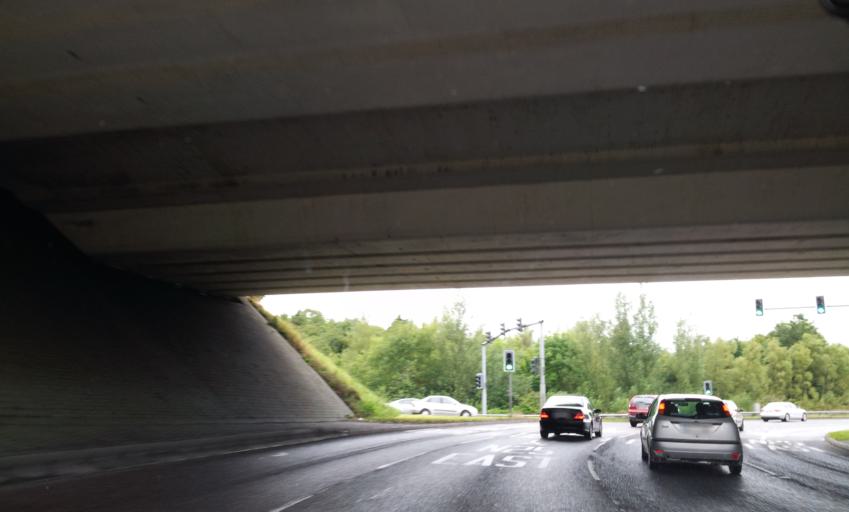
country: IE
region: Munster
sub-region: County Cork
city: Passage West
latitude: 51.9043
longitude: -8.3886
